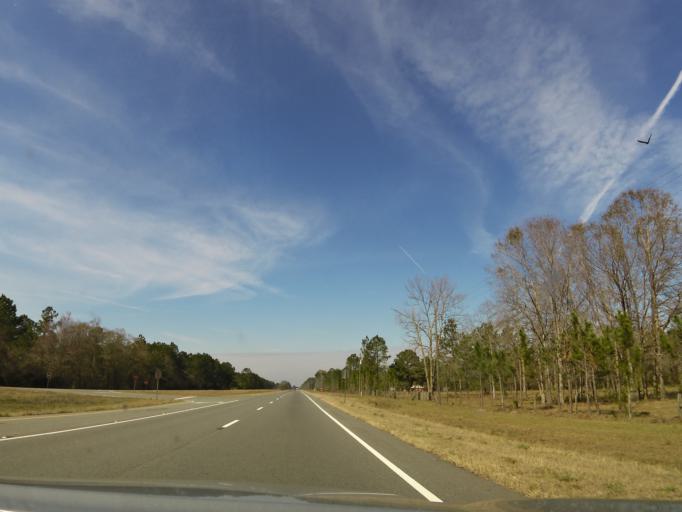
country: US
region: Georgia
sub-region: Ware County
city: Waycross
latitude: 31.0805
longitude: -82.2060
